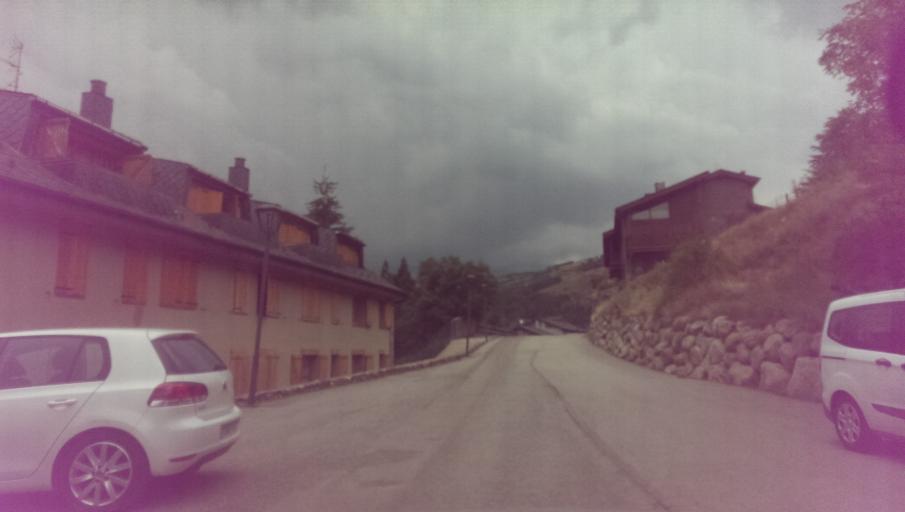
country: ES
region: Catalonia
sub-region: Provincia de Girona
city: Llivia
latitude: 42.4659
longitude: 1.9821
